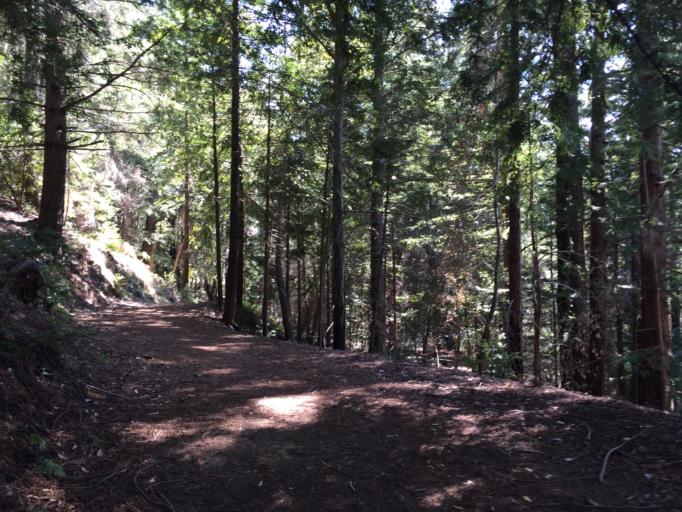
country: US
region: California
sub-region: Santa Cruz County
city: Boulder Creek
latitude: 37.1936
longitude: -122.2317
